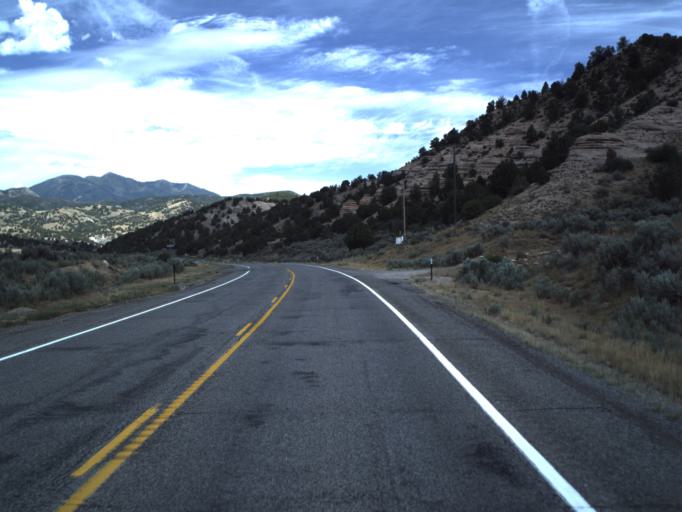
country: US
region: Utah
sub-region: Utah County
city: Woodland Hills
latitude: 39.9236
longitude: -111.5445
